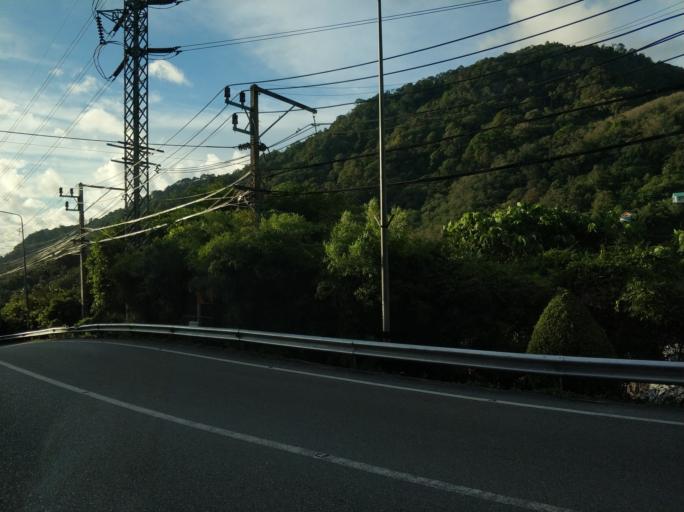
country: TH
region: Phuket
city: Kathu
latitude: 7.9030
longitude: 98.3184
